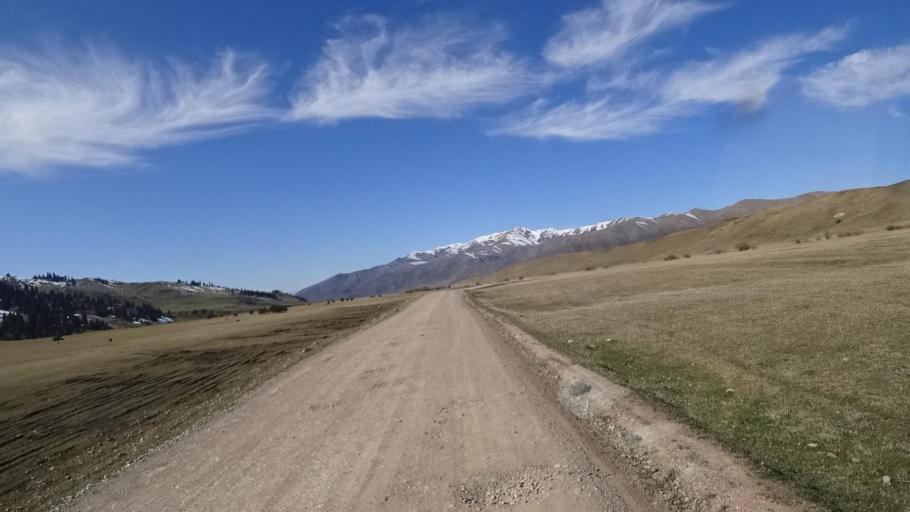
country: KZ
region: Almaty Oblysy
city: Kegen
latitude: 42.7294
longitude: 79.0420
